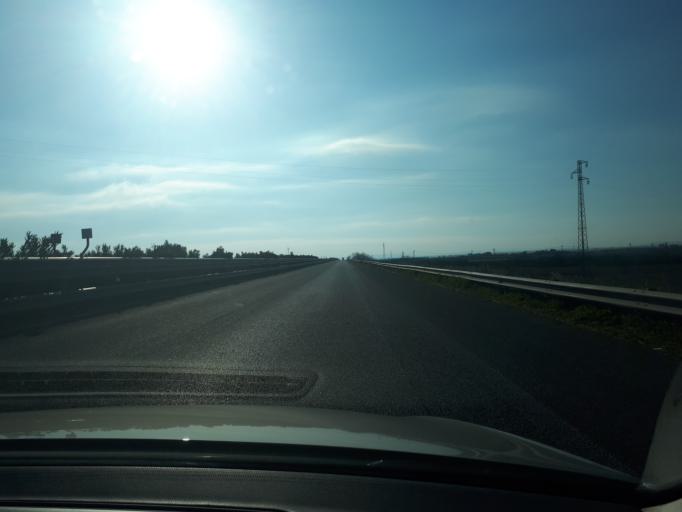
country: IT
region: Apulia
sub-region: Provincia di Foggia
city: Foggia
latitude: 41.4125
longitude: 15.5585
